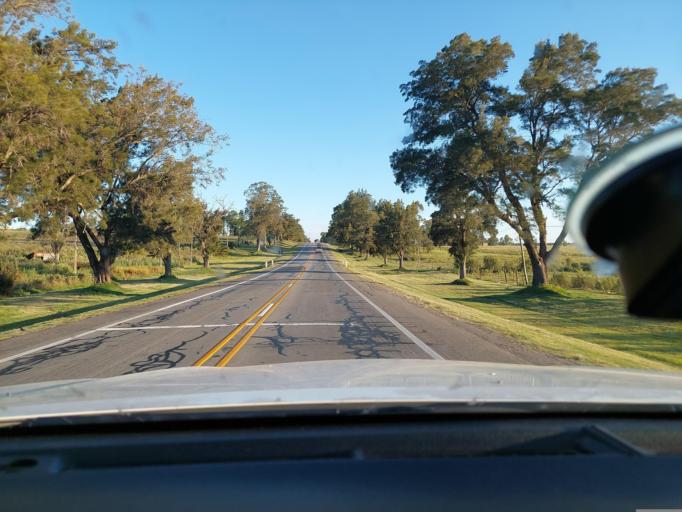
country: UY
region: Canelones
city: San Jacinto
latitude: -34.5513
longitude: -55.8684
